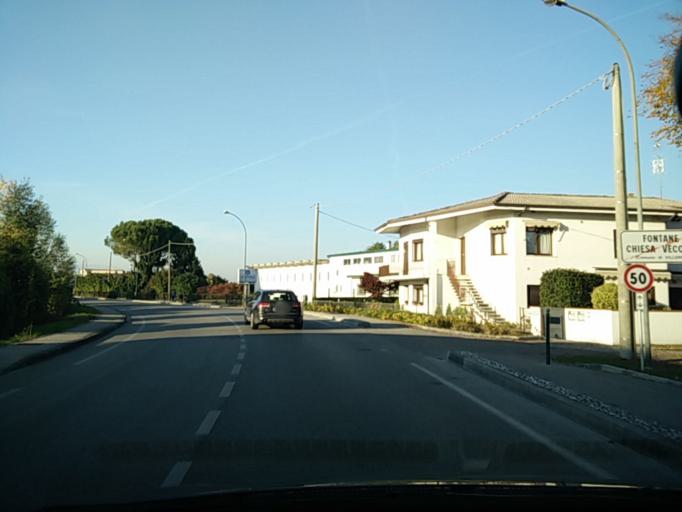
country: IT
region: Veneto
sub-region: Provincia di Treviso
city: Lancenigo-Villorba
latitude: 45.6977
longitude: 12.2496
